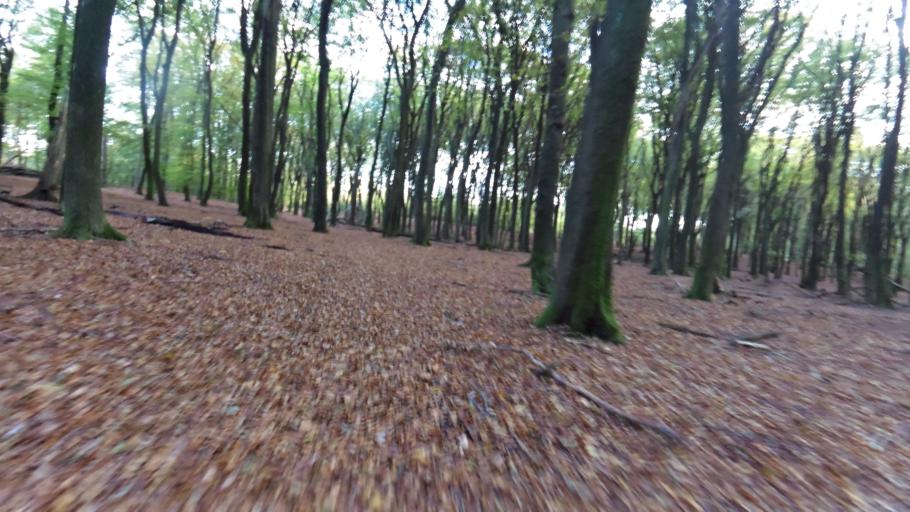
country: NL
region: Gelderland
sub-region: Gemeente Apeldoorn
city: Uddel
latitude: 52.3146
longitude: 5.8347
